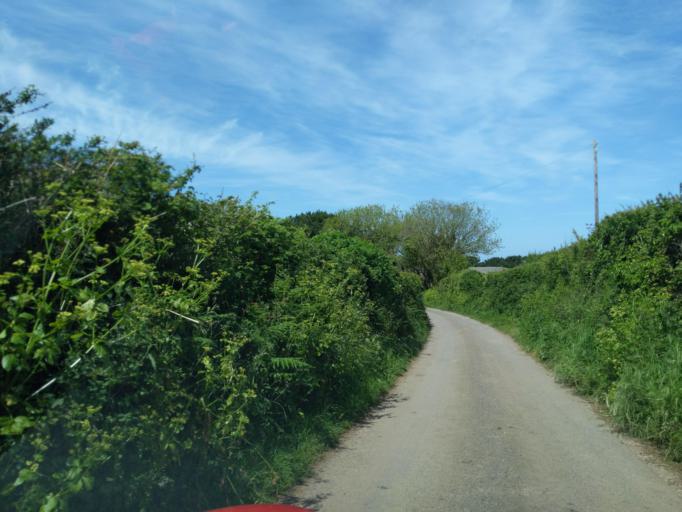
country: GB
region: England
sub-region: Borough of Torbay
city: Brixham
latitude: 50.3612
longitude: -3.5311
